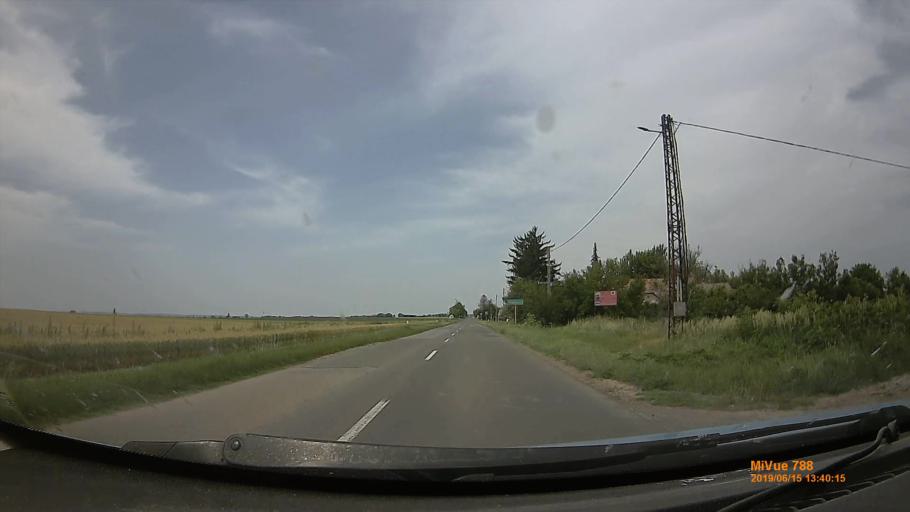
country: HU
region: Tolna
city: Iregszemcse
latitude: 46.6404
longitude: 18.1973
